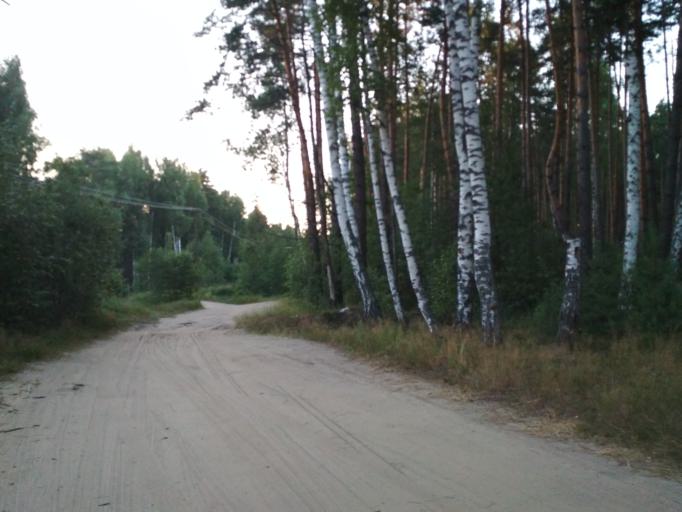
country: RU
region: Rjazan
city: Solotcha
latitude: 54.8269
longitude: 39.9446
